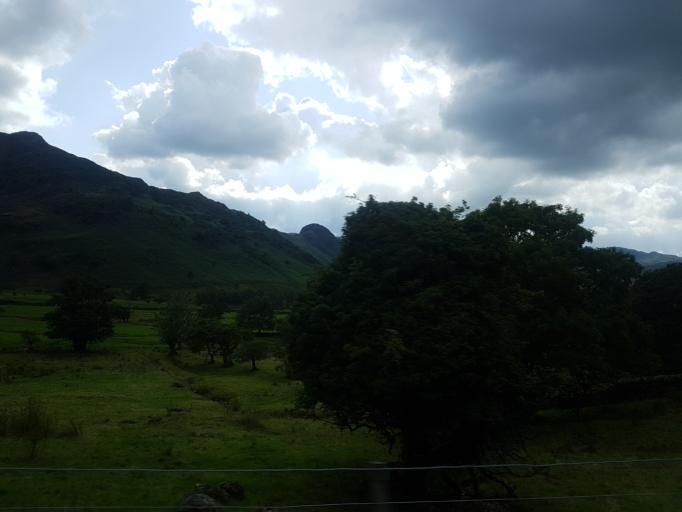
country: GB
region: England
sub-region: Cumbria
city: Ambleside
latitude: 54.4501
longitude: -3.0705
